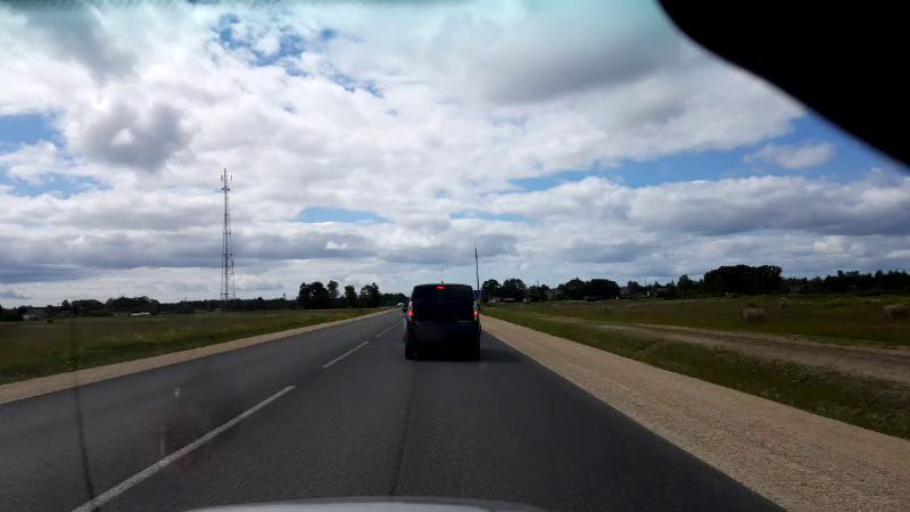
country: LV
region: Salacgrivas
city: Ainazi
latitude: 57.8637
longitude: 24.3703
